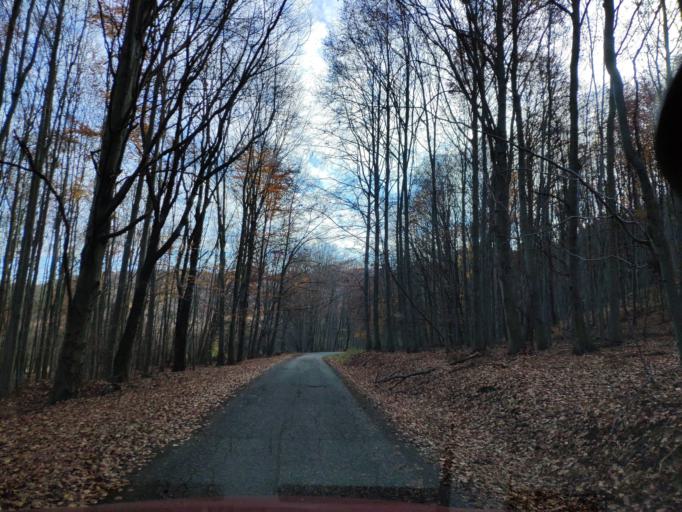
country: HU
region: Borsod-Abauj-Zemplen
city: Gonc
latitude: 48.5940
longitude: 21.4521
